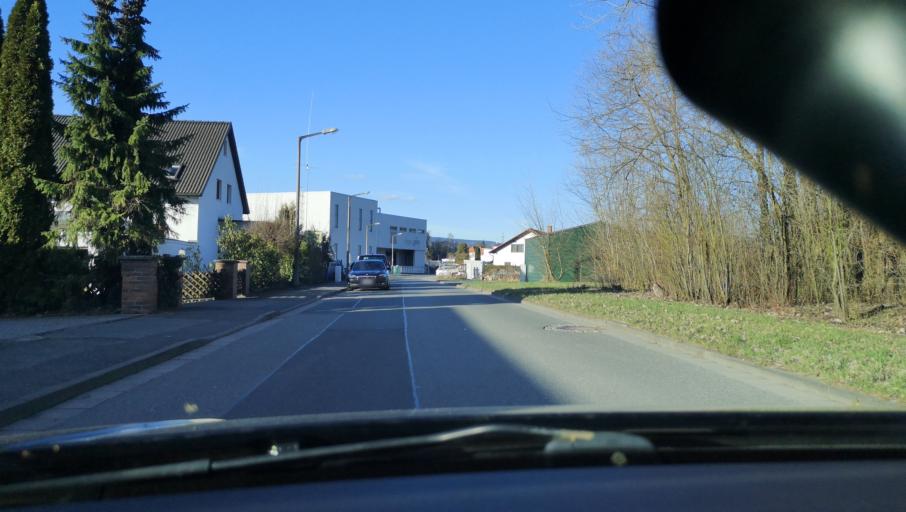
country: DE
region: Bavaria
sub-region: Upper Franconia
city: Neustadt bei Coburg
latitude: 50.3221
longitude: 11.1103
